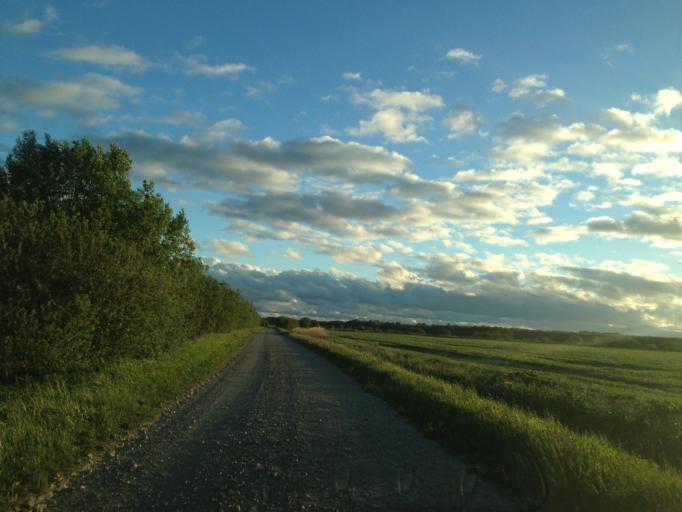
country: EE
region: Raplamaa
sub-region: Maerjamaa vald
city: Marjamaa
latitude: 58.7582
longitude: 24.1894
